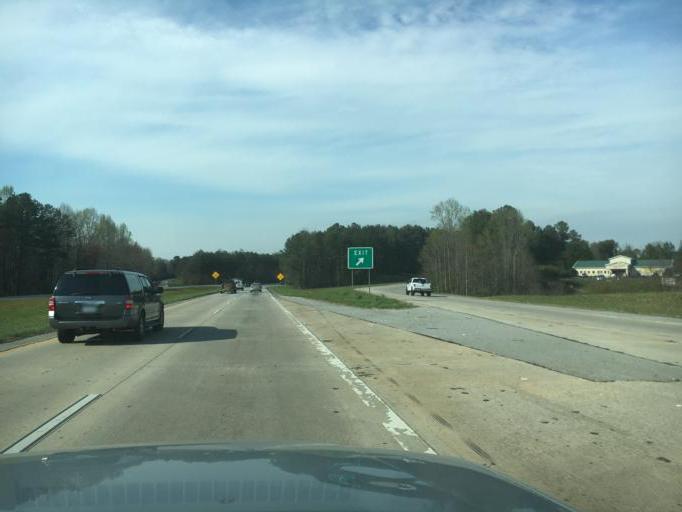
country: US
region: Georgia
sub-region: Habersham County
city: Cornelia
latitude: 34.5334
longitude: -83.5406
